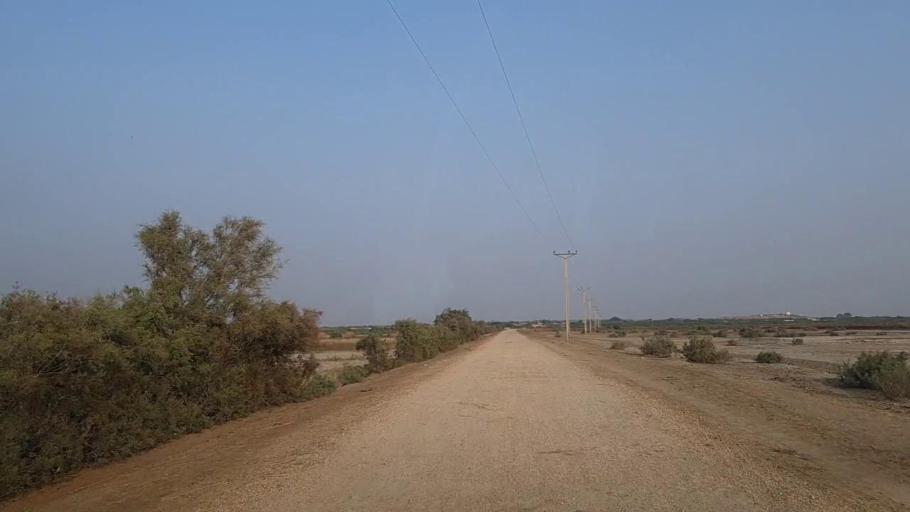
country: PK
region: Sindh
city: Thatta
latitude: 24.6903
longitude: 67.8102
